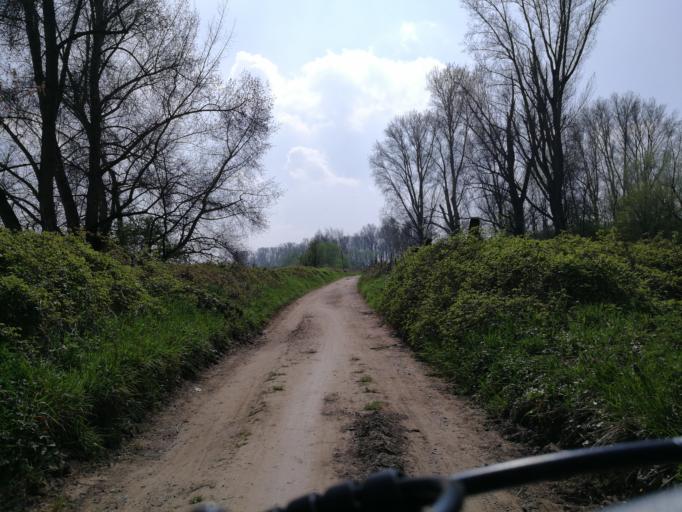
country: DE
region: North Rhine-Westphalia
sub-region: Regierungsbezirk Dusseldorf
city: Dormagen
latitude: 51.1445
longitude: 6.8470
